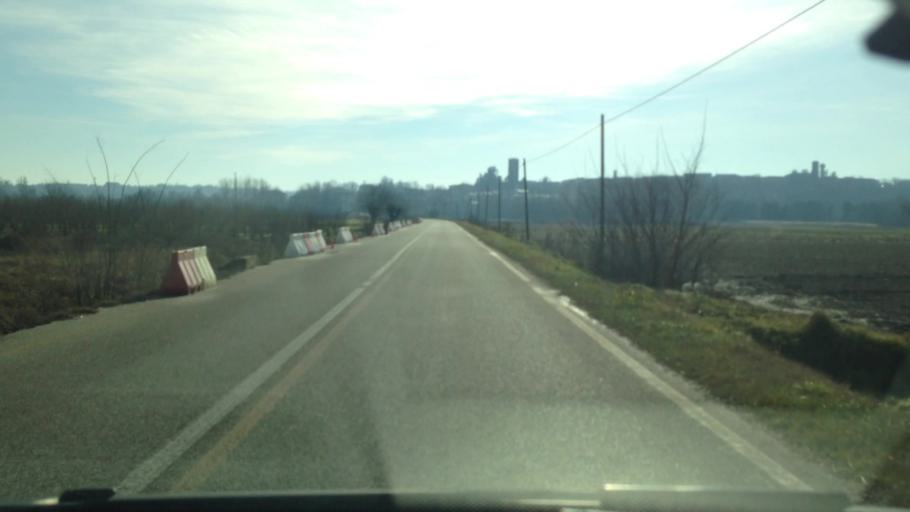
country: IT
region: Piedmont
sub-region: Provincia di Alessandria
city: Masio
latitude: 44.8786
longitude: 8.4093
